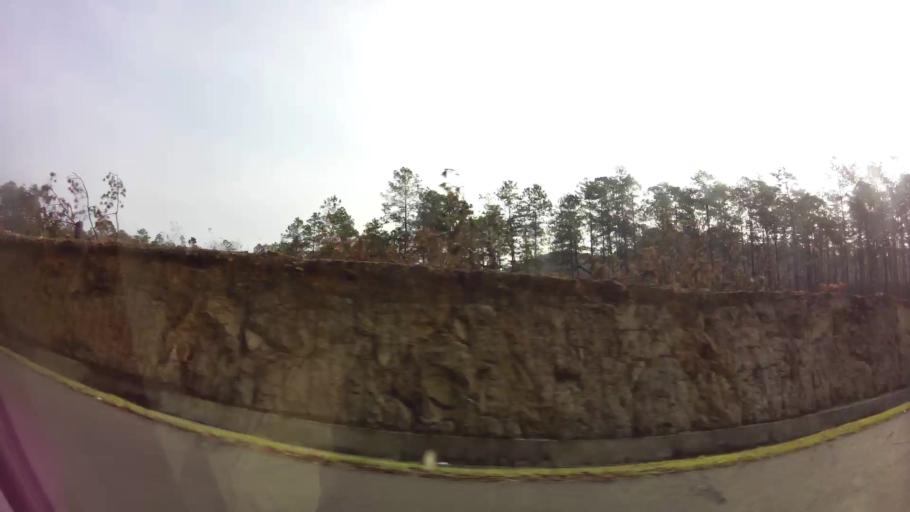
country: HN
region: Francisco Morazan
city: Zambrano
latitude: 14.2909
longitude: -87.4244
